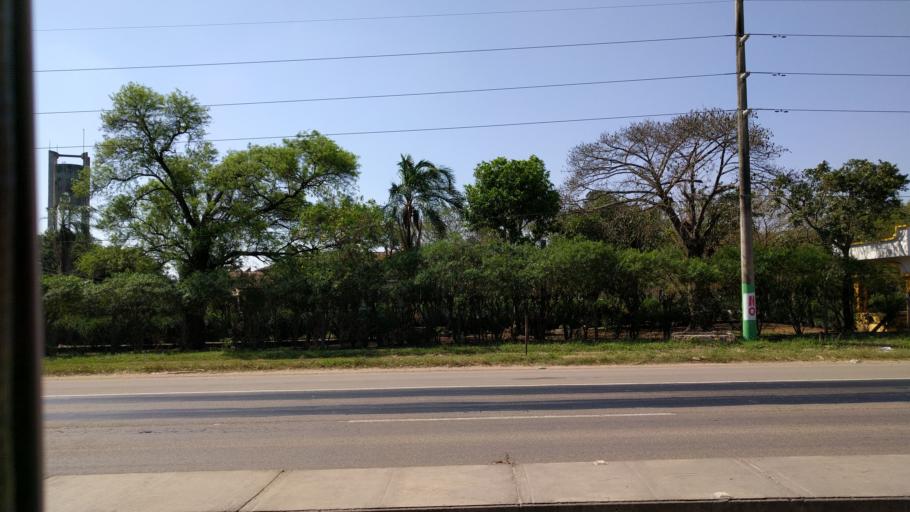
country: BO
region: Santa Cruz
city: Cotoca
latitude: -17.7645
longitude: -63.0625
